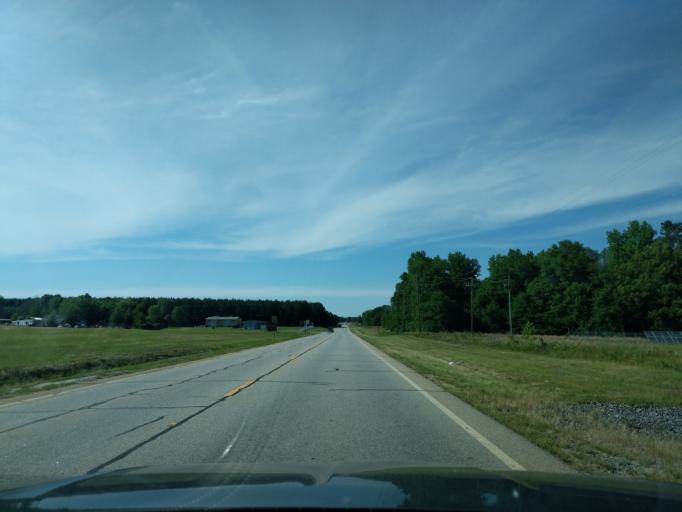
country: US
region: Georgia
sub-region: Jefferson County
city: Wrens
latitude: 33.2219
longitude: -82.3784
